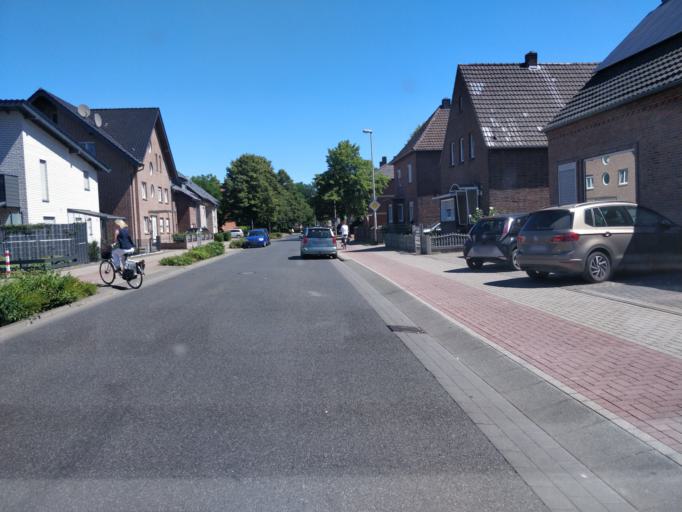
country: DE
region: North Rhine-Westphalia
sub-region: Regierungsbezirk Dusseldorf
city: Emmerich
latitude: 51.8419
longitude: 6.2503
